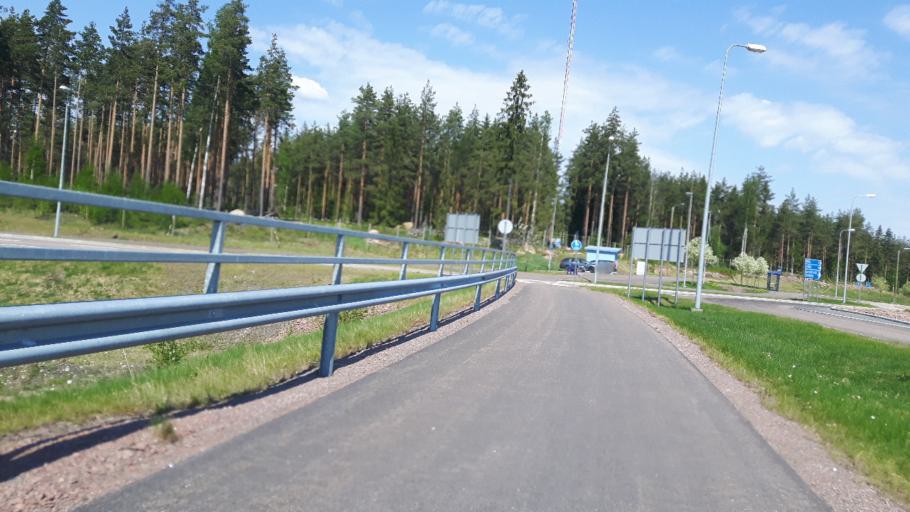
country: FI
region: Uusimaa
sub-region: Loviisa
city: Ruotsinpyhtaeae
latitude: 60.4927
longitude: 26.4193
